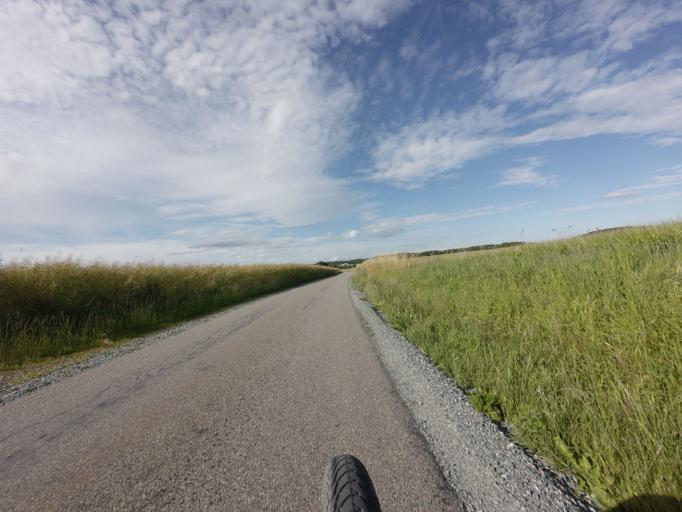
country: DK
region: Central Jutland
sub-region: Skanderborg Kommune
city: Stilling
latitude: 56.0855
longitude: 9.9666
